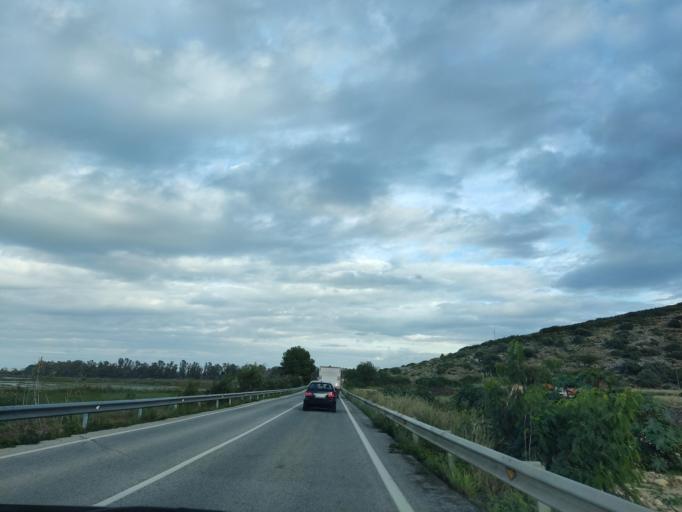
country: ES
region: Valencia
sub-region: Provincia de Alicante
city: Benimeli
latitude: 38.8535
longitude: -0.0313
